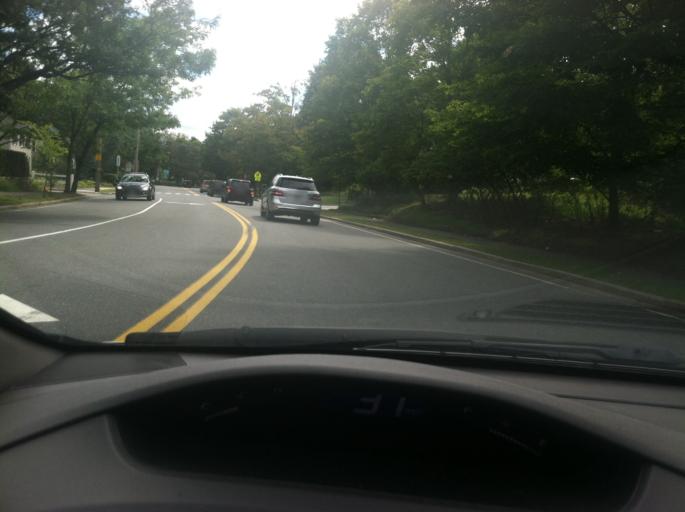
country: US
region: Massachusetts
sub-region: Middlesex County
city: Lexington
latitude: 42.4360
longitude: -71.2123
